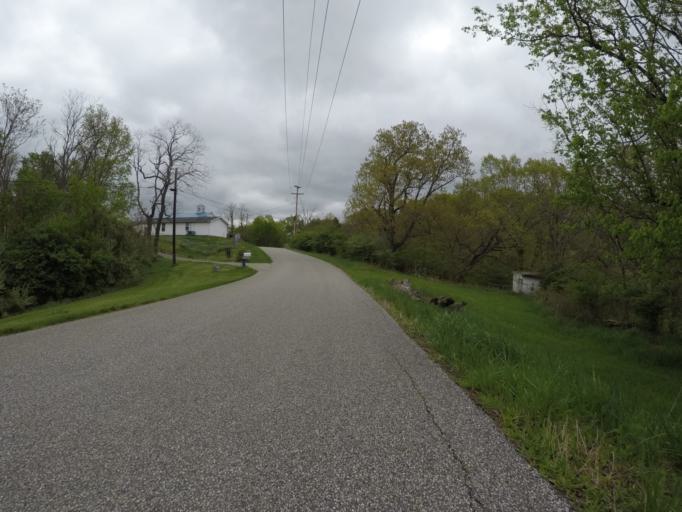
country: US
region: West Virginia
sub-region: Cabell County
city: Barboursville
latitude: 38.4020
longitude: -82.2656
